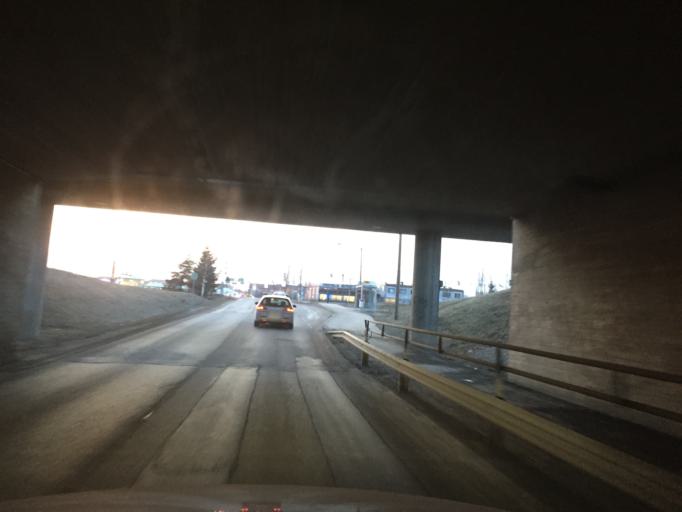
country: FI
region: Uusimaa
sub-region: Helsinki
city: Vantaa
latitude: 60.2820
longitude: 24.9786
